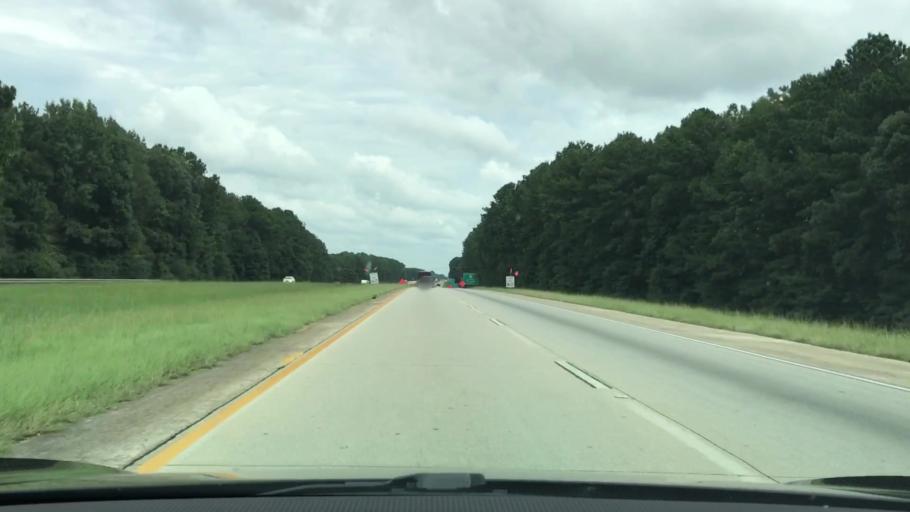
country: US
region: Georgia
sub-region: Troup County
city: La Grange
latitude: 33.0228
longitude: -84.9843
